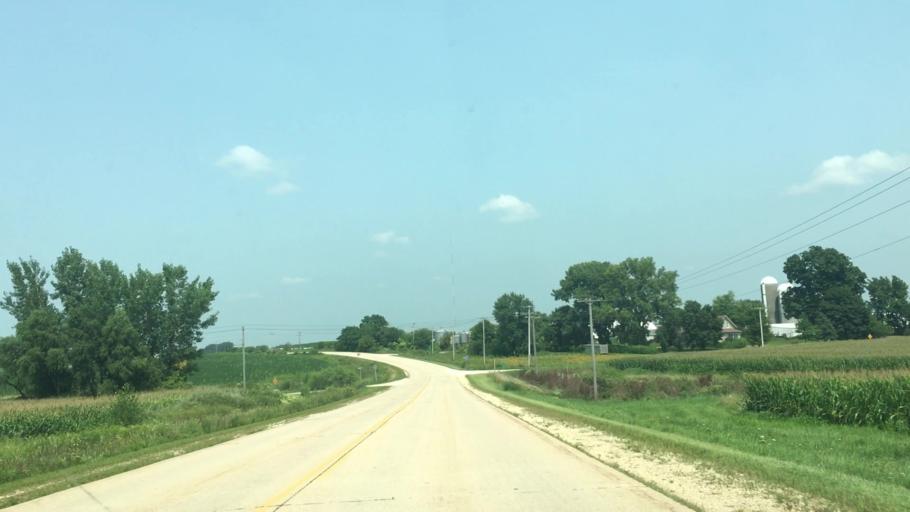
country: US
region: Iowa
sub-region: Fayette County
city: Oelwein
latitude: 42.6634
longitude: -91.8956
